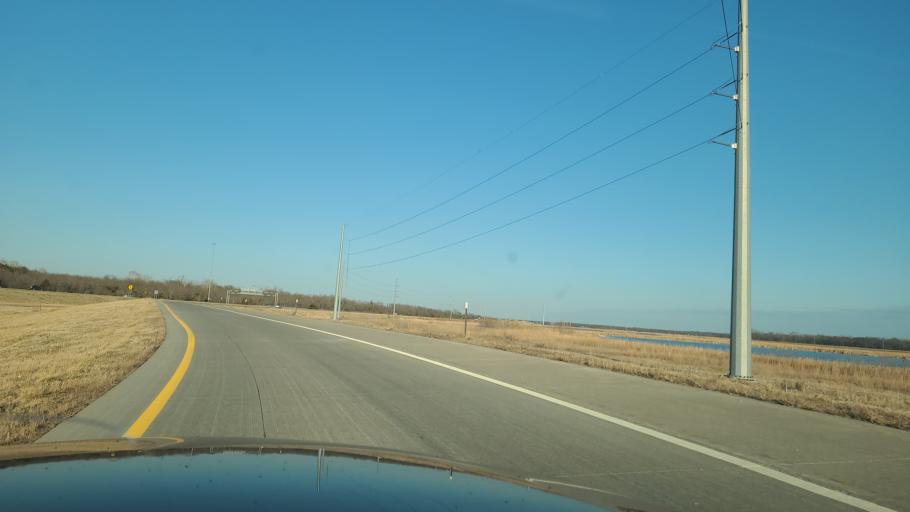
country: US
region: Kansas
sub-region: Douglas County
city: Lawrence
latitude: 38.9230
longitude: -95.2179
